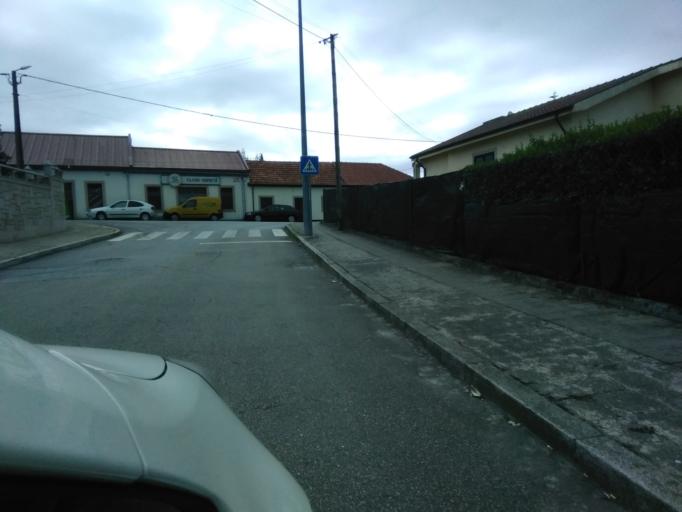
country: PT
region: Porto
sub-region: Valongo
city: Valongo
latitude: 41.1892
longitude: -8.4893
